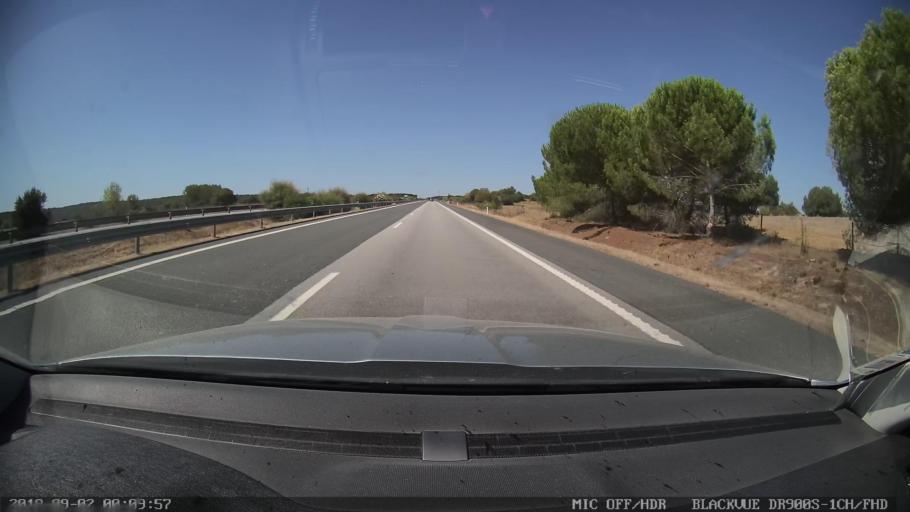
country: PT
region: Evora
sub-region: Evora
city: Evora
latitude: 38.6294
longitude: -7.9498
